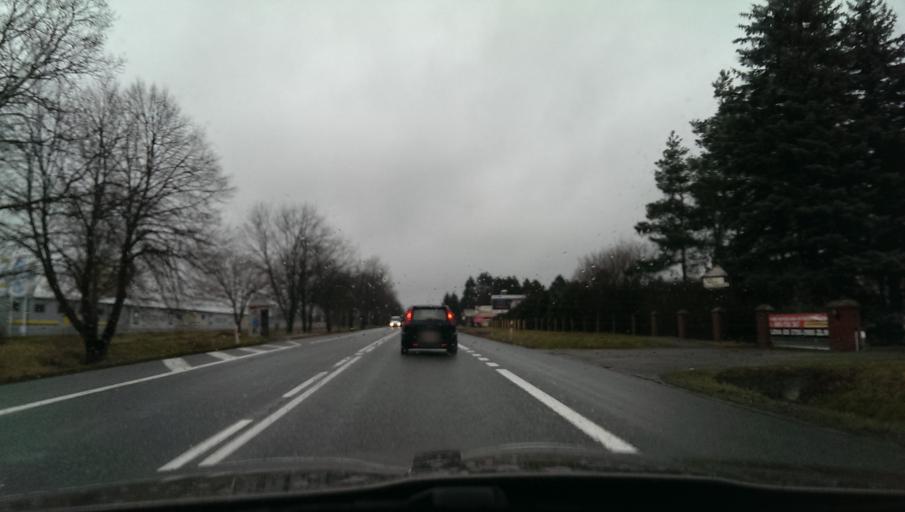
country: PL
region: Subcarpathian Voivodeship
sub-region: Powiat rzeszowski
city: Rudna Mala
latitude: 50.1016
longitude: 21.9779
